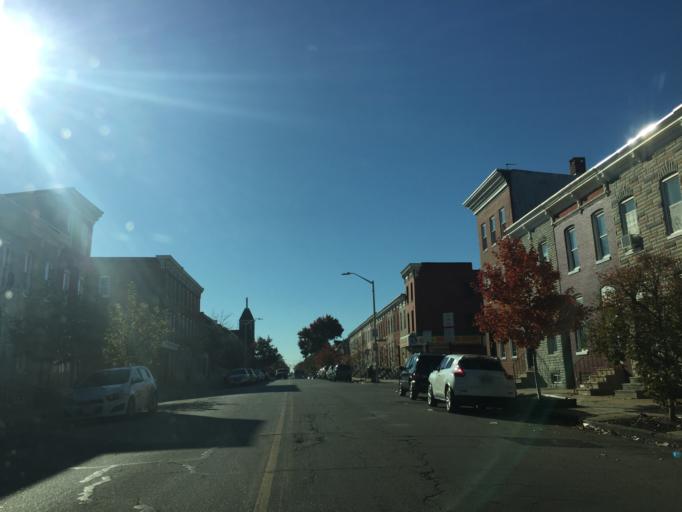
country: US
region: Maryland
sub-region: City of Baltimore
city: Baltimore
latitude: 39.2971
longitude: -76.5850
